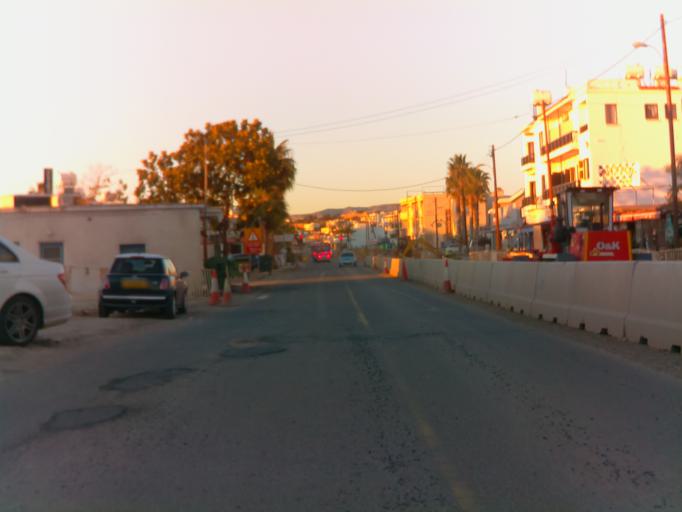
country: CY
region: Pafos
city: Paphos
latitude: 34.7671
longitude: 32.4105
